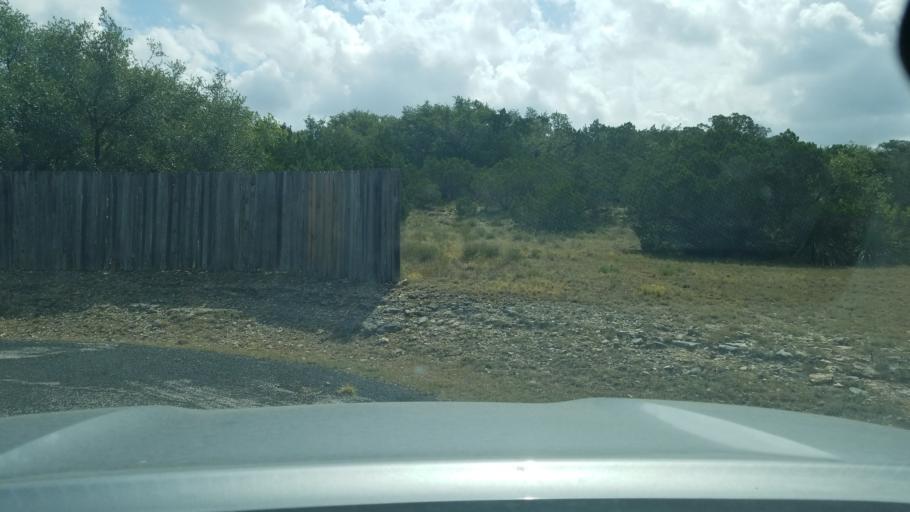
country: US
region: Texas
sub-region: Bexar County
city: Timberwood Park
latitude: 29.6737
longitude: -98.5194
